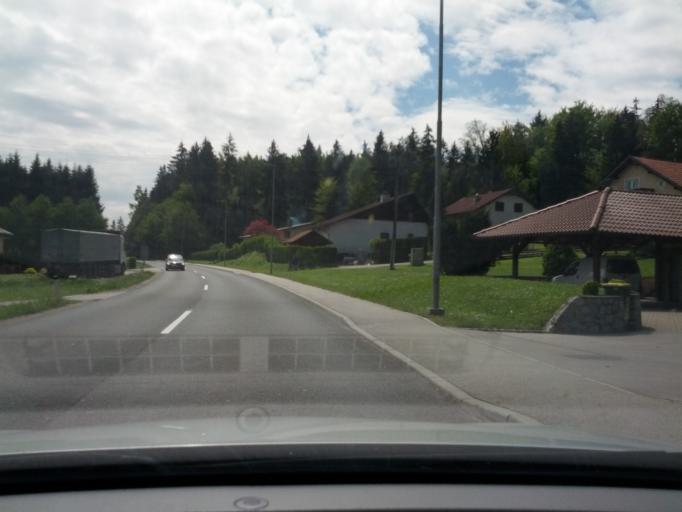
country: SI
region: Sentjur pri Celju
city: Sentjur
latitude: 46.2557
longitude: 15.3866
